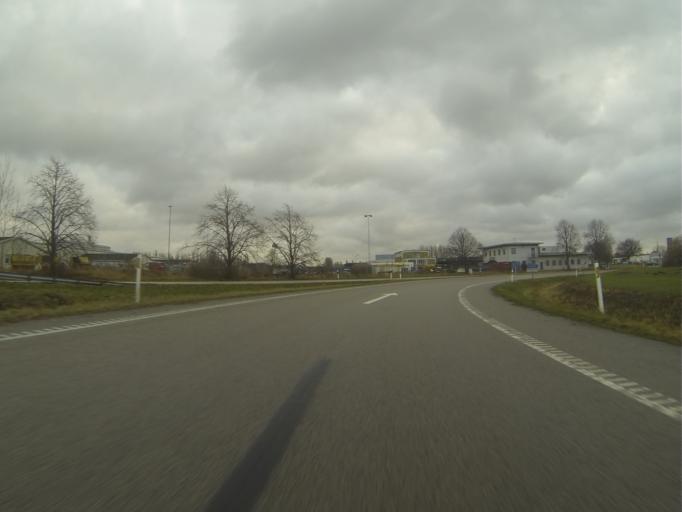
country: SE
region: Skane
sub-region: Burlovs Kommun
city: Arloev
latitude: 55.6474
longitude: 13.0829
